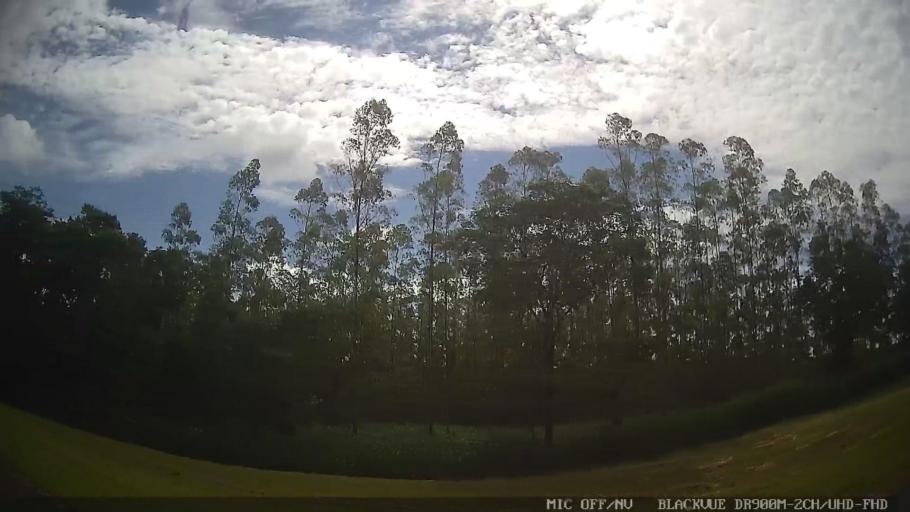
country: BR
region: Sao Paulo
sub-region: Laranjal Paulista
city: Laranjal Paulista
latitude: -23.0604
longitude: -47.8229
